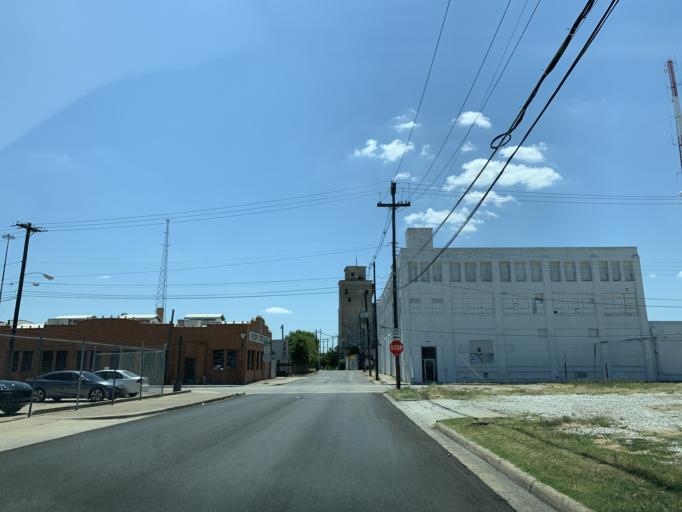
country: US
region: Texas
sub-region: Dallas County
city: Dallas
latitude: 32.7828
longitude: -96.7725
